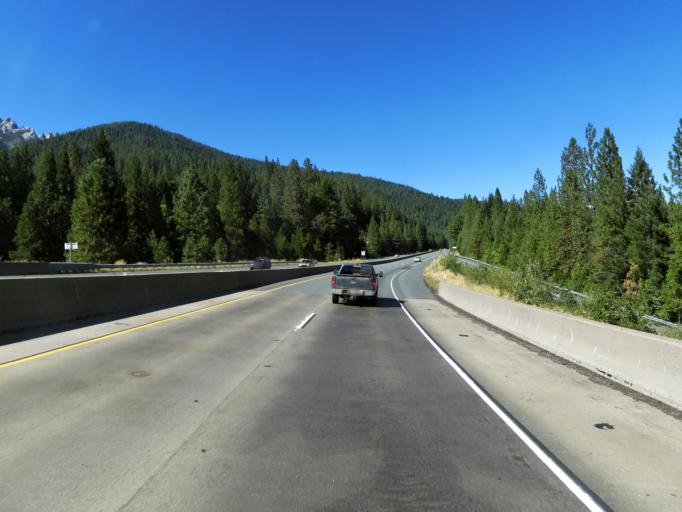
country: US
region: California
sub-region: Siskiyou County
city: Dunsmuir
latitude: 41.1625
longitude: -122.2973
